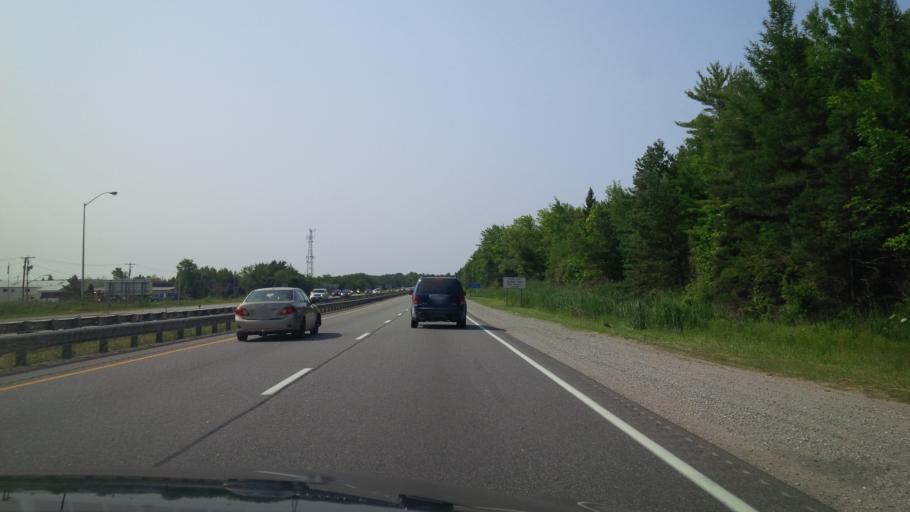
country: CA
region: Ontario
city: Orillia
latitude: 44.5728
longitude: -79.4438
